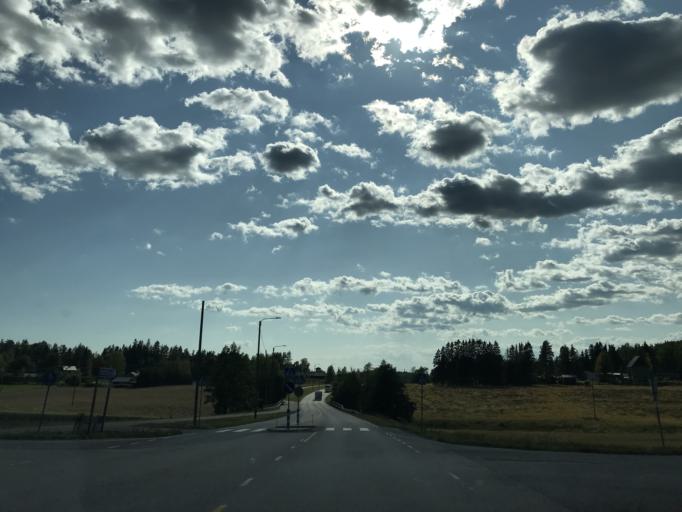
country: FI
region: Uusimaa
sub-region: Helsinki
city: Nurmijaervi
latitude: 60.4628
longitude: 24.7906
